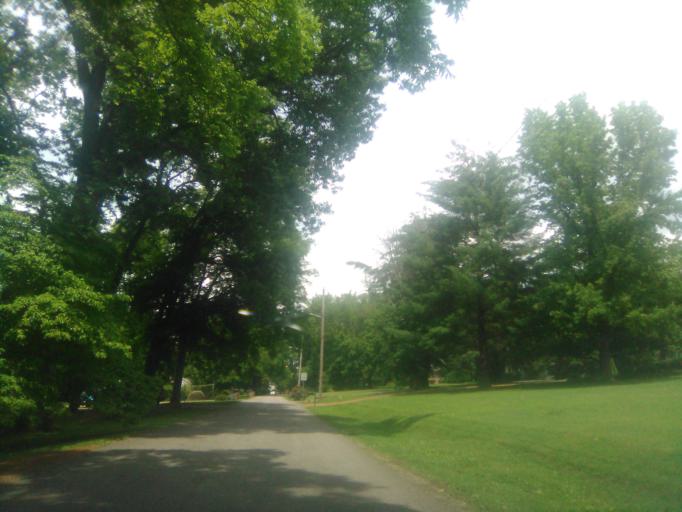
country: US
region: Tennessee
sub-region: Davidson County
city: Belle Meade
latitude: 36.0908
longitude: -86.8669
